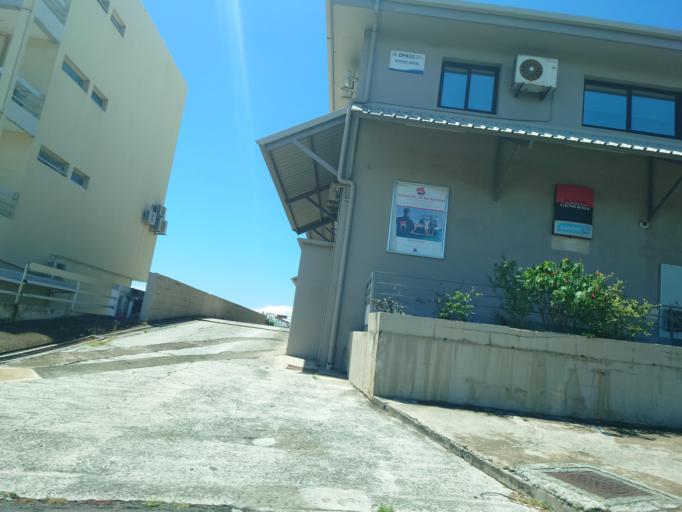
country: NC
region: South Province
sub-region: Noumea
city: Noumea
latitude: -22.2690
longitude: 166.4608
